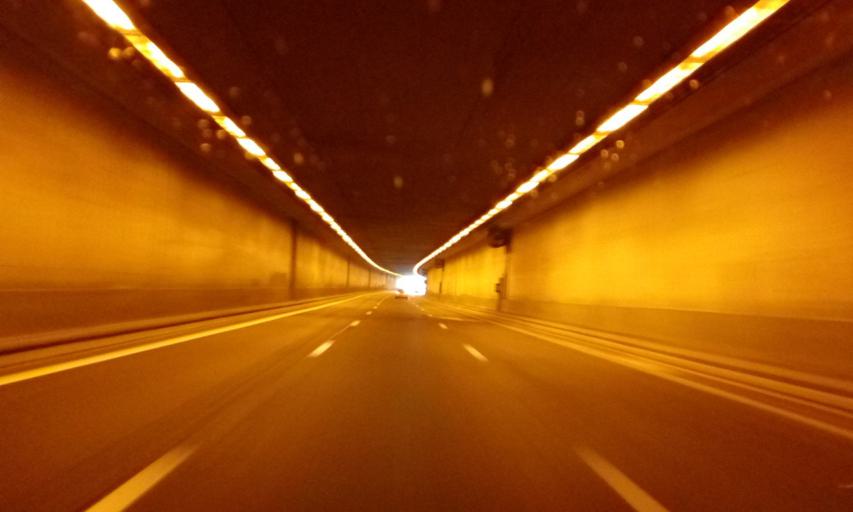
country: BE
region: Wallonia
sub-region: Province du Hainaut
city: Charleroi
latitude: 50.3838
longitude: 4.4565
